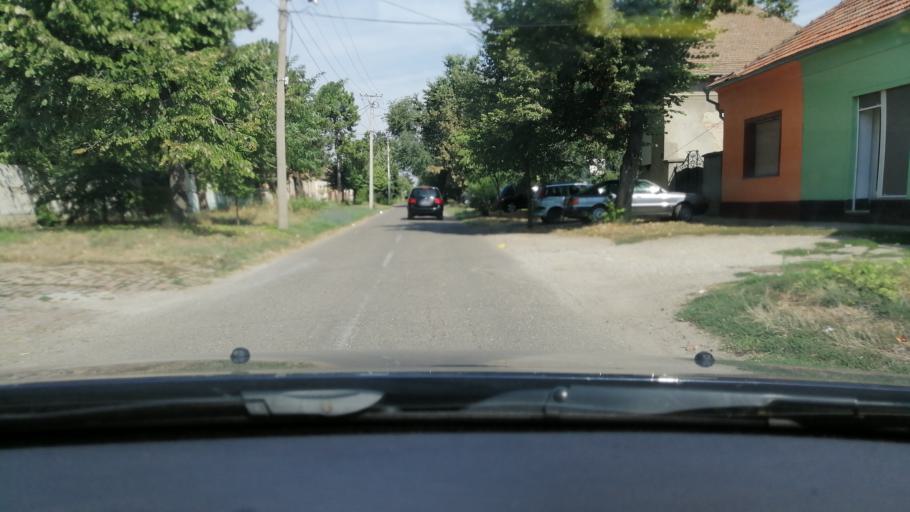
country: RS
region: Autonomna Pokrajina Vojvodina
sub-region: Srednjebanatski Okrug
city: Zrenjanin
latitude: 45.3856
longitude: 20.3775
